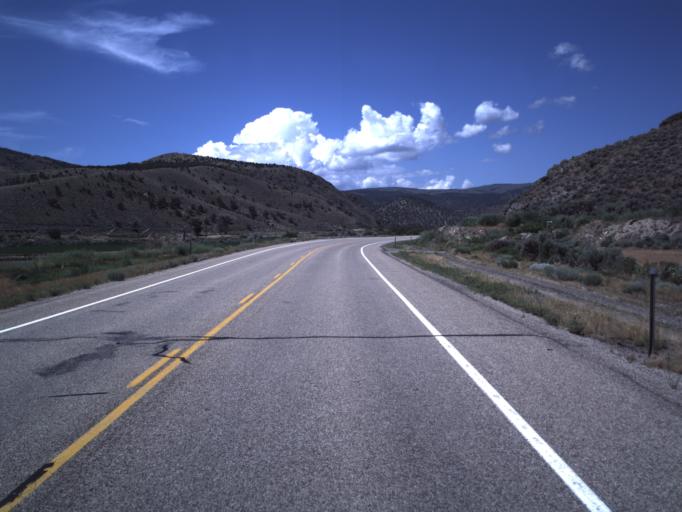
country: US
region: Utah
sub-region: Piute County
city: Junction
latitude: 38.1545
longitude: -112.2844
